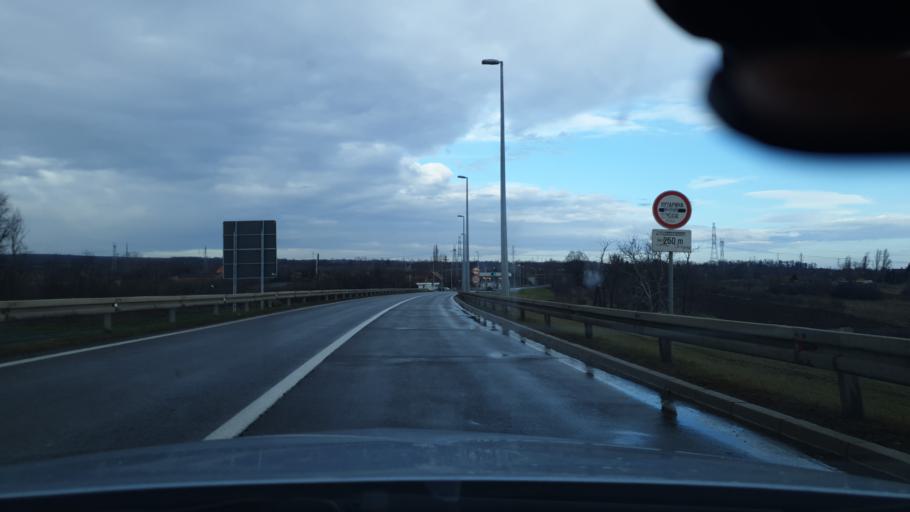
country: RS
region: Central Serbia
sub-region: Podunavski Okrug
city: Smederevo
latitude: 44.5878
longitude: 20.9583
